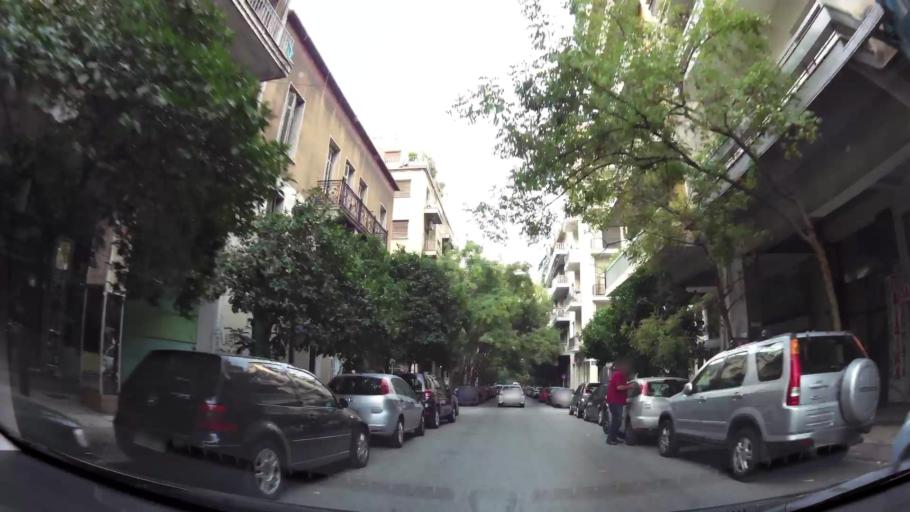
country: GR
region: Attica
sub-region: Nomarchia Athinas
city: Kipseli
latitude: 37.9845
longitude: 23.7390
